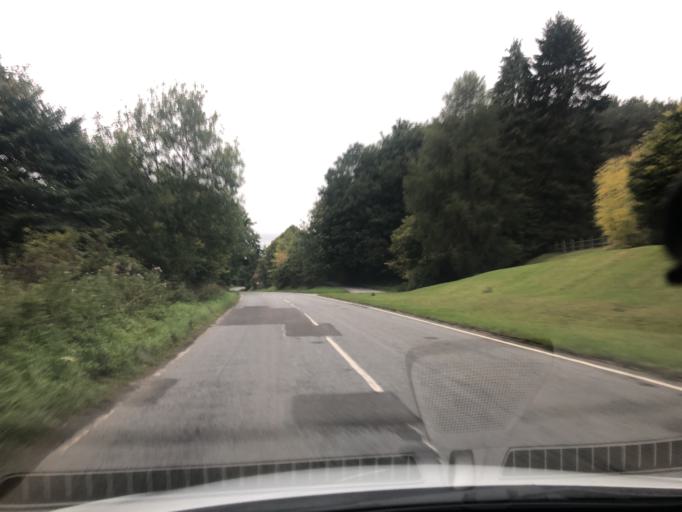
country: GB
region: Scotland
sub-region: Perth and Kinross
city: Pitlochry
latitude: 56.7509
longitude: -3.7980
